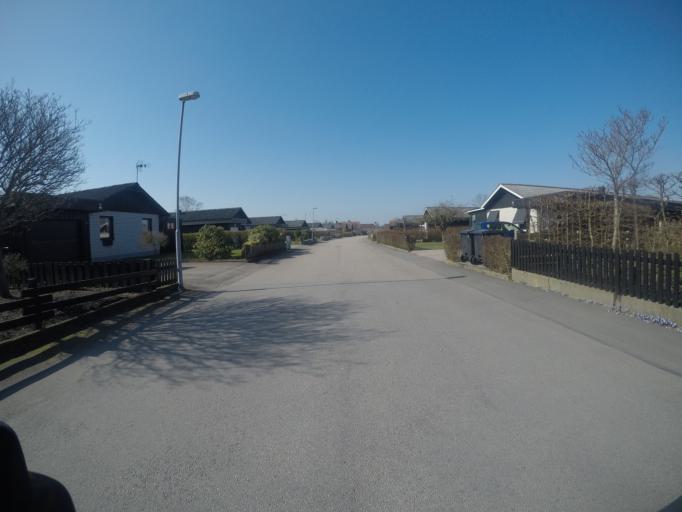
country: SE
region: Halland
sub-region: Laholms Kommun
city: Laholm
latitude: 56.5018
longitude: 13.0442
